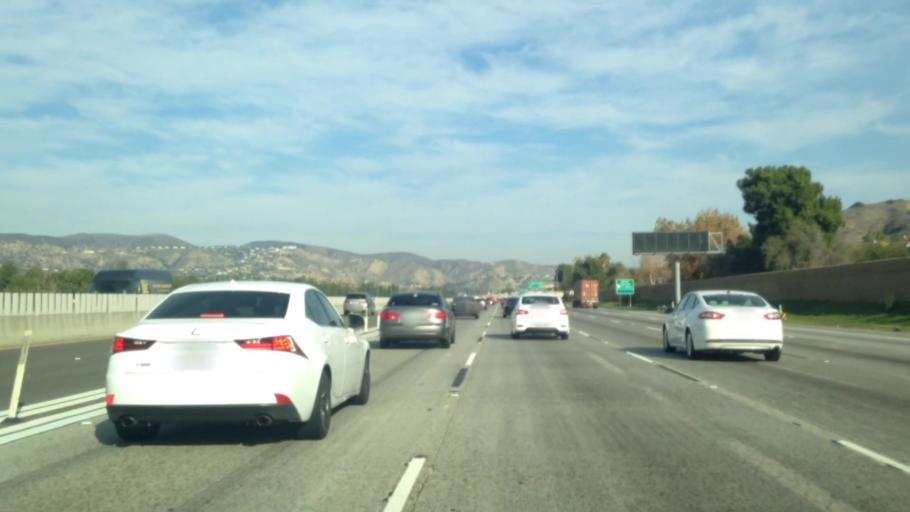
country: US
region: California
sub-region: Orange County
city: Yorba Linda
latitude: 33.8641
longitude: -117.7686
